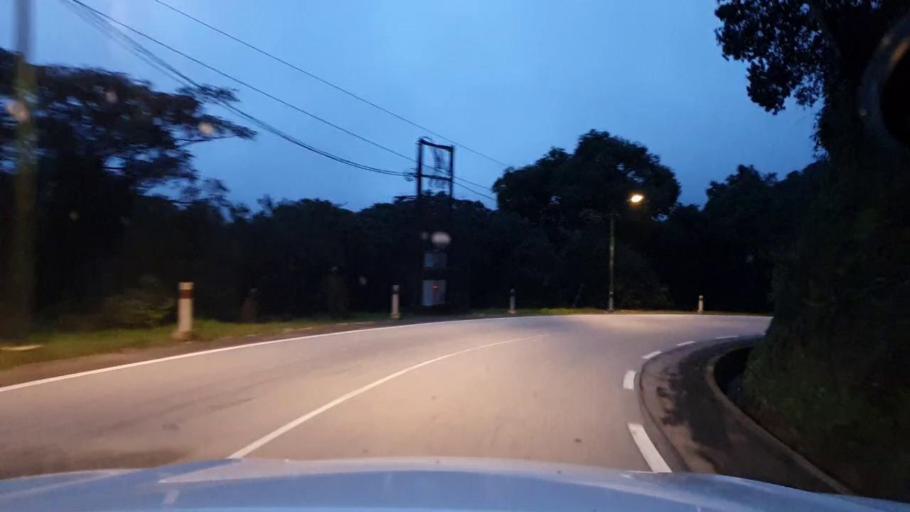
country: RW
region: Southern Province
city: Nzega
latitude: -2.5301
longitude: 29.3832
